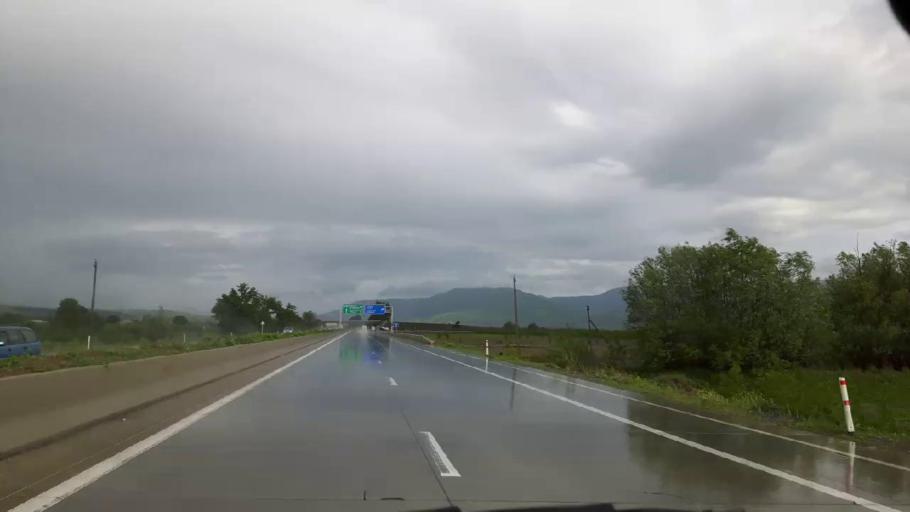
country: GE
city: Agara
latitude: 42.0339
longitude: 43.9438
